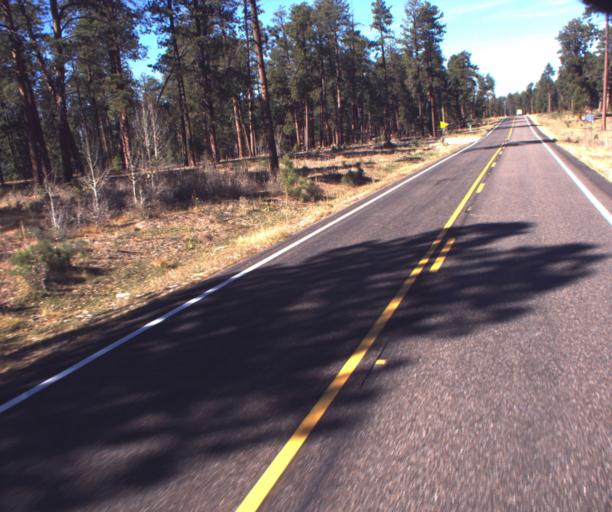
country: US
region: Arizona
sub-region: Coconino County
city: Fredonia
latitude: 36.6591
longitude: -112.1895
